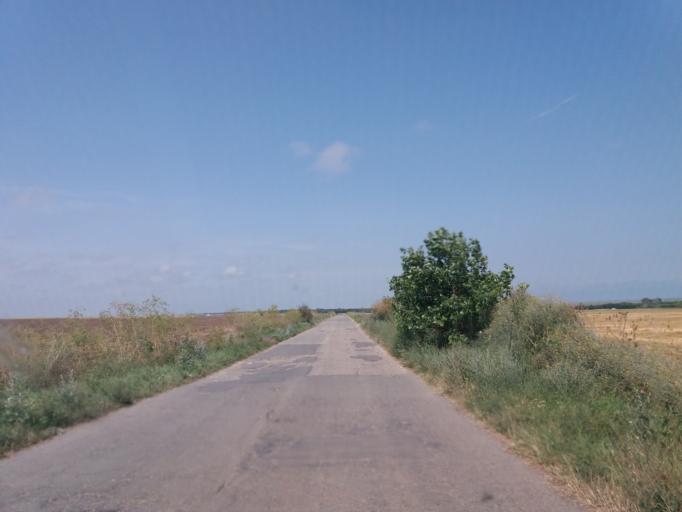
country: RO
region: Constanta
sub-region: Comuna Corbu
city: Corbu
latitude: 44.4268
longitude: 28.7138
